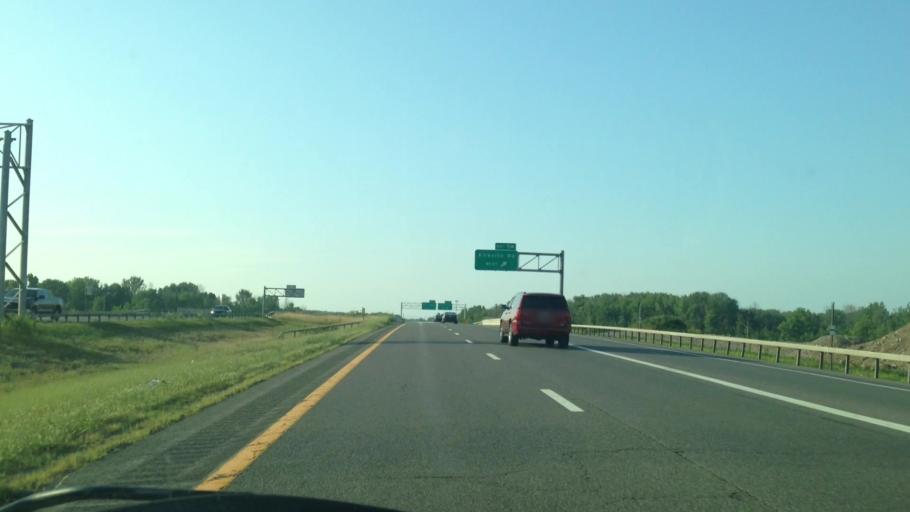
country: US
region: New York
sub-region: Onondaga County
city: East Syracuse
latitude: 43.0761
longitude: -76.0534
